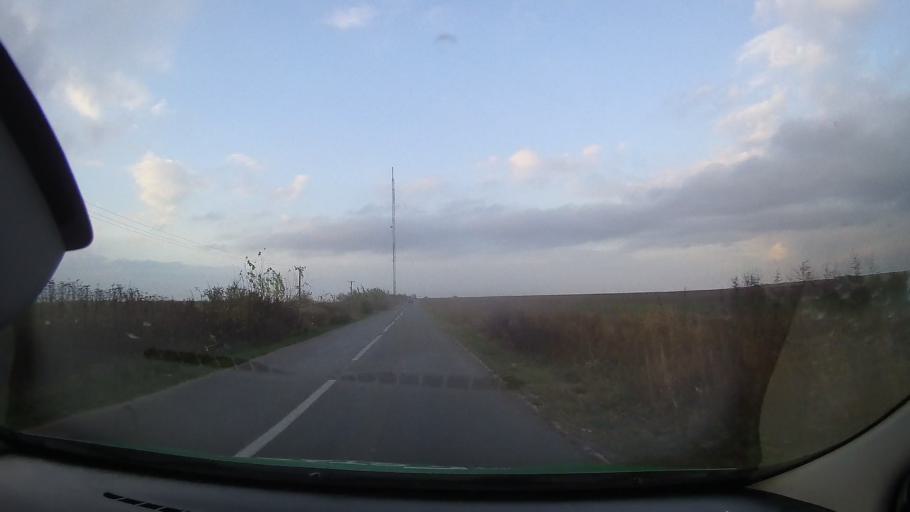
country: RO
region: Constanta
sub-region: Comuna Dobromir
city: Dobromir
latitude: 44.0447
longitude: 27.7546
